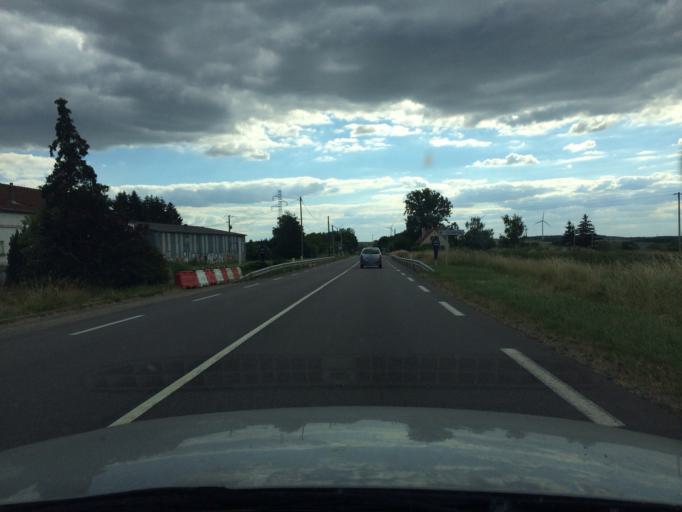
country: FR
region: Lorraine
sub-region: Departement de la Moselle
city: Lorquin
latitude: 48.6419
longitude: 6.9100
